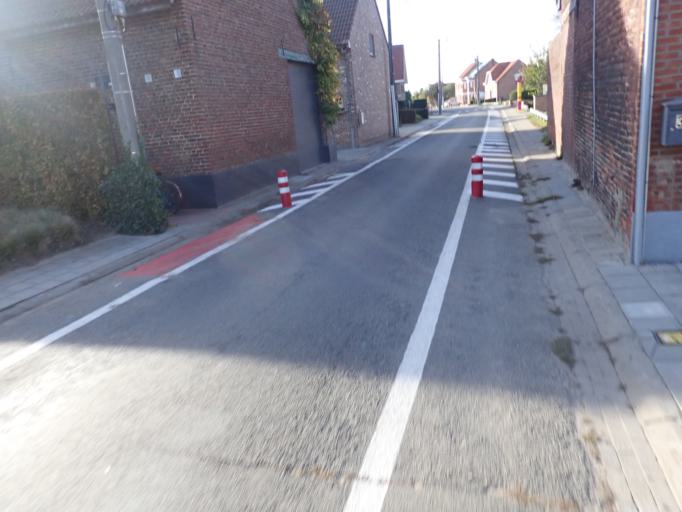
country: BE
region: Flanders
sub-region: Provincie Vlaams-Brabant
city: Rotselaar
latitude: 50.9539
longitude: 4.7121
